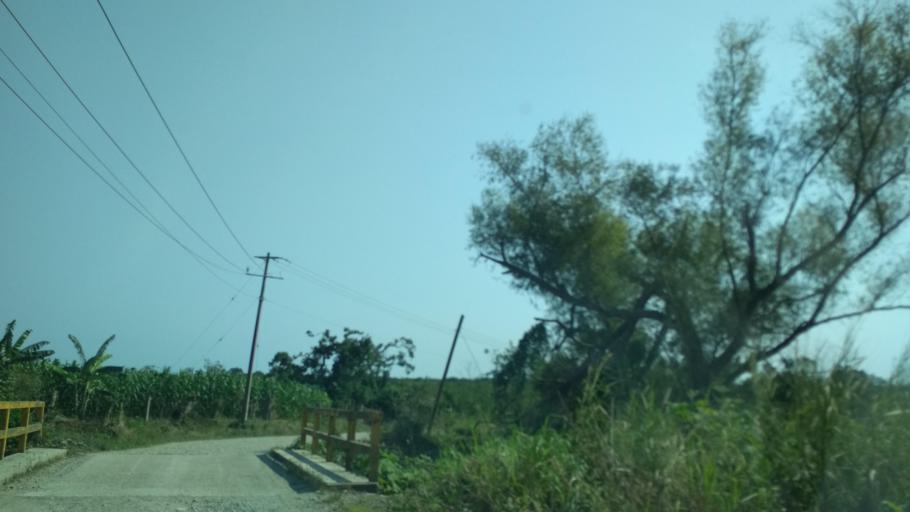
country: MX
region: Veracruz
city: Gutierrez Zamora
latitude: 20.4123
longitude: -97.1866
